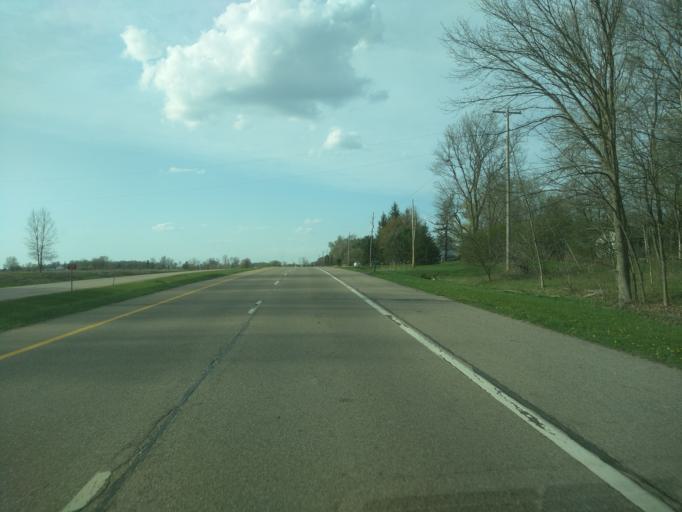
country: US
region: Michigan
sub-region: Eaton County
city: Dimondale
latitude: 42.6331
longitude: -84.6228
